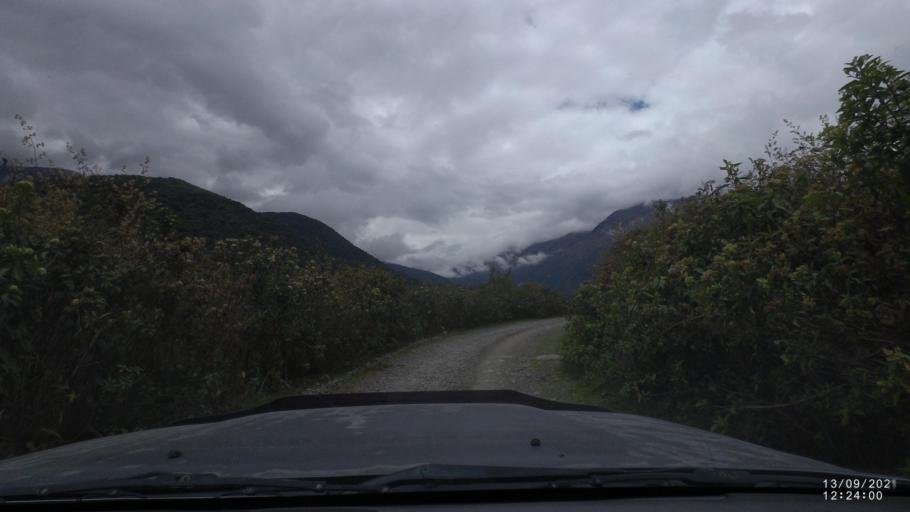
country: BO
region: Cochabamba
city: Colomi
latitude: -17.2446
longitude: -65.8183
